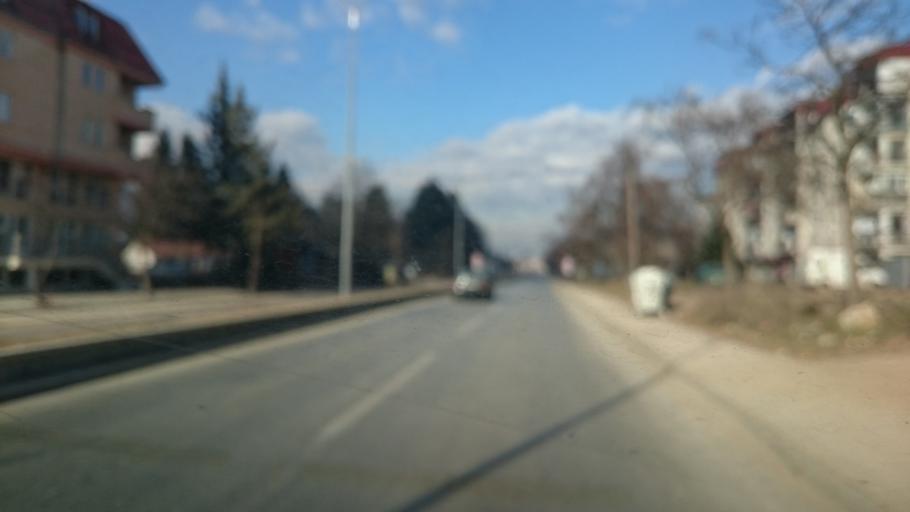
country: MK
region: Kicevo
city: Kicevo
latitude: 41.5045
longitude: 20.9525
